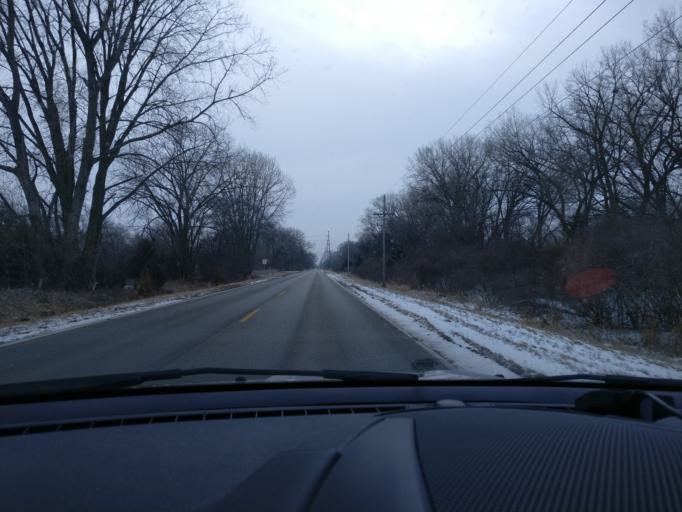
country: US
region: Nebraska
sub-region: Dodge County
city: Fremont
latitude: 41.4437
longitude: -96.5393
